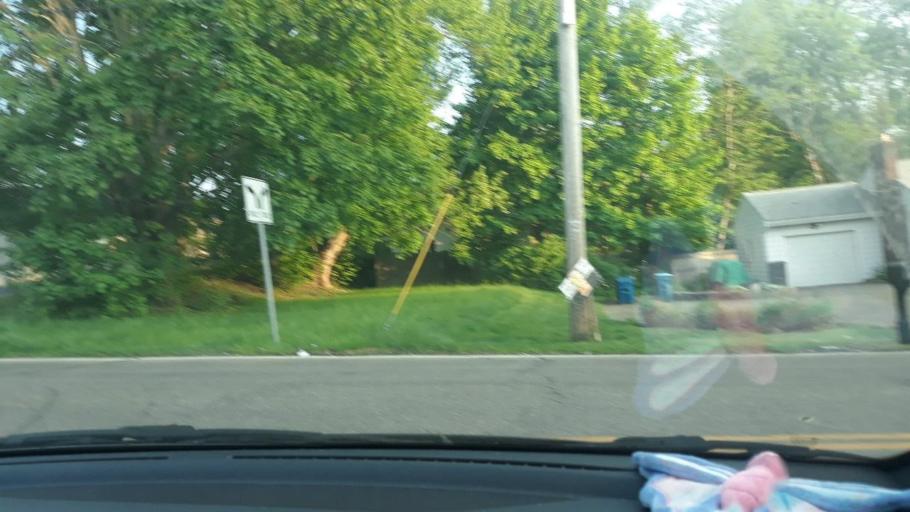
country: US
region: Ohio
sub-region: Summit County
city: Portage Lakes
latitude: 41.0018
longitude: -81.5245
